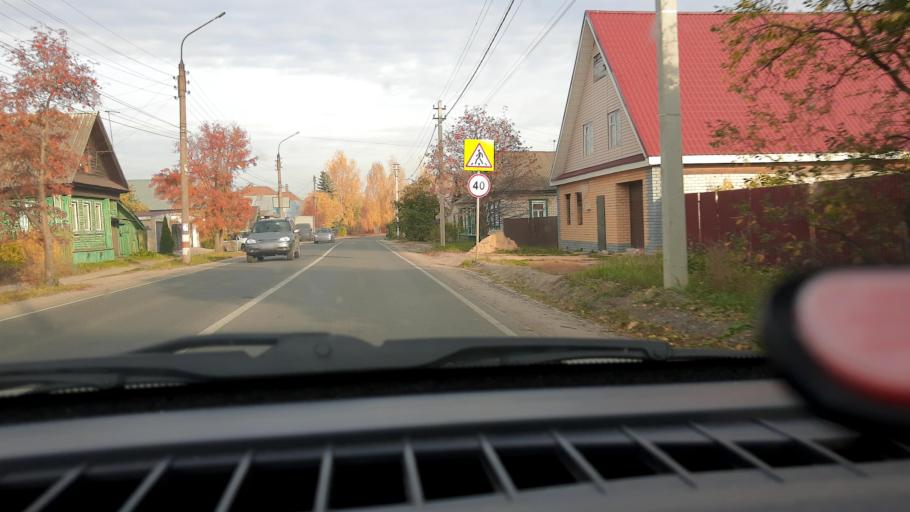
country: RU
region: Nizjnij Novgorod
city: Gorodets
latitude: 56.6457
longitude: 43.4814
